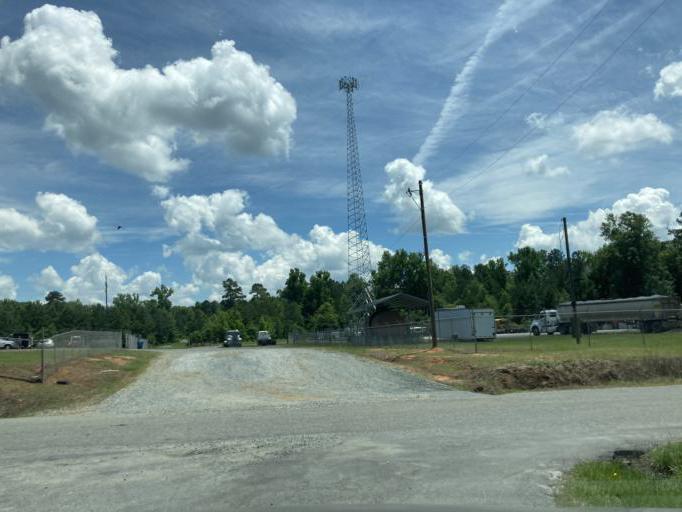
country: US
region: Georgia
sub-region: Jones County
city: Gray
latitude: 32.9171
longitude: -83.5180
